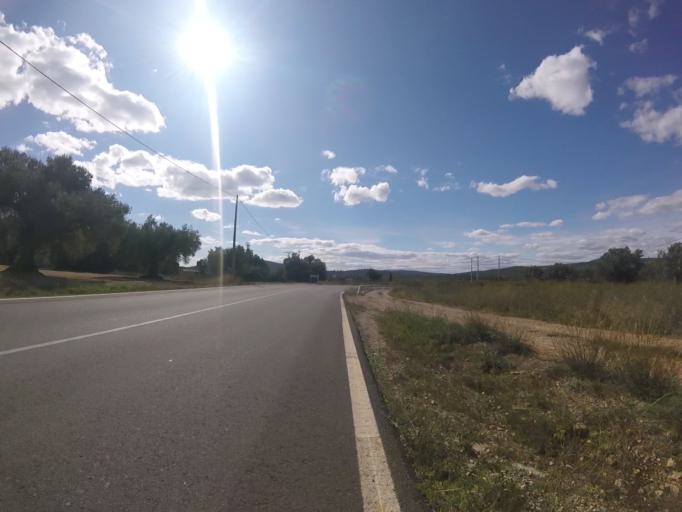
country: ES
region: Valencia
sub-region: Provincia de Castello
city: Chert/Xert
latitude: 40.4275
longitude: 0.1558
